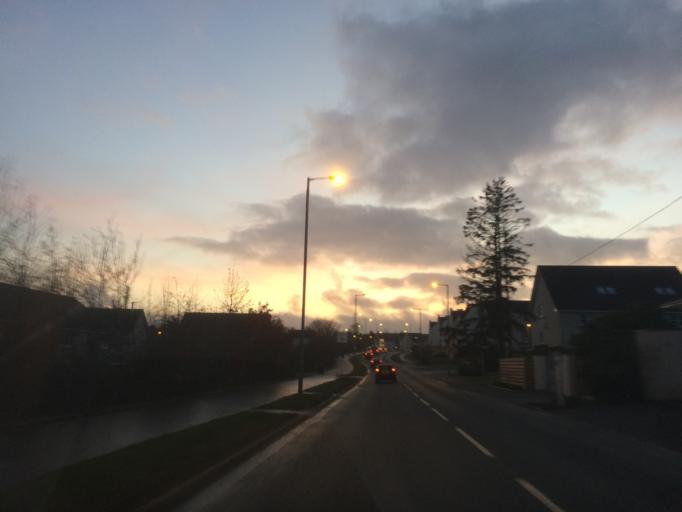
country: GB
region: Scotland
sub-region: East Renfrewshire
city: Newton Mearns
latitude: 55.7889
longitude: -4.3391
